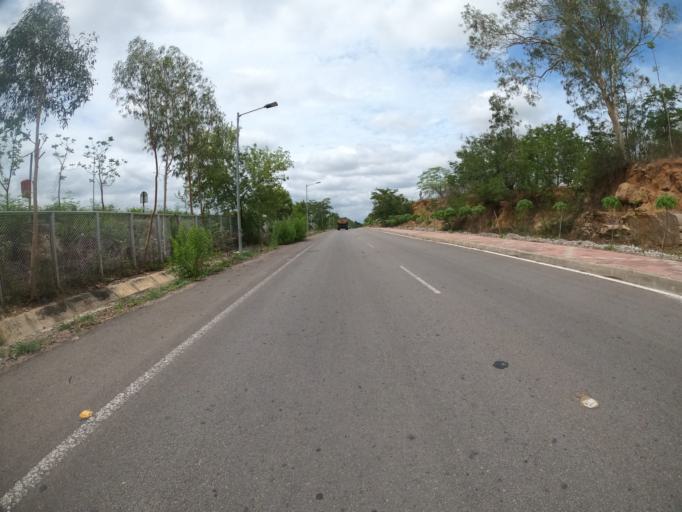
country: IN
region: Telangana
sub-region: Rangareddi
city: Balapur
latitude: 17.2763
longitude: 78.3817
